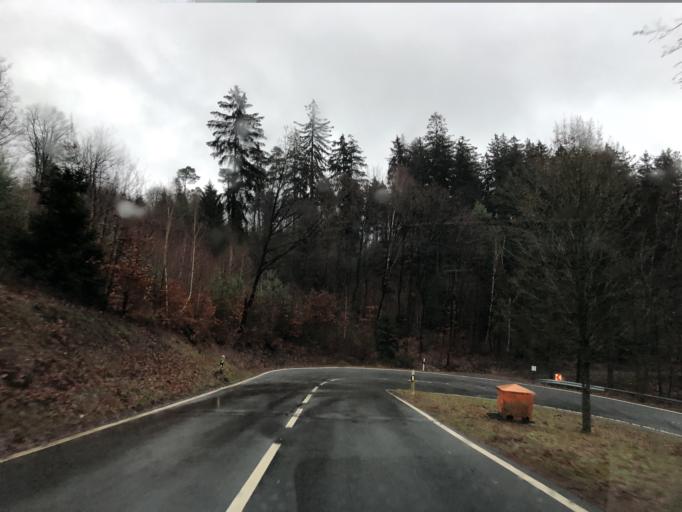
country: DE
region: Hesse
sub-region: Regierungsbezirk Darmstadt
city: Lutzelbach
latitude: 49.7151
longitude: 9.0787
